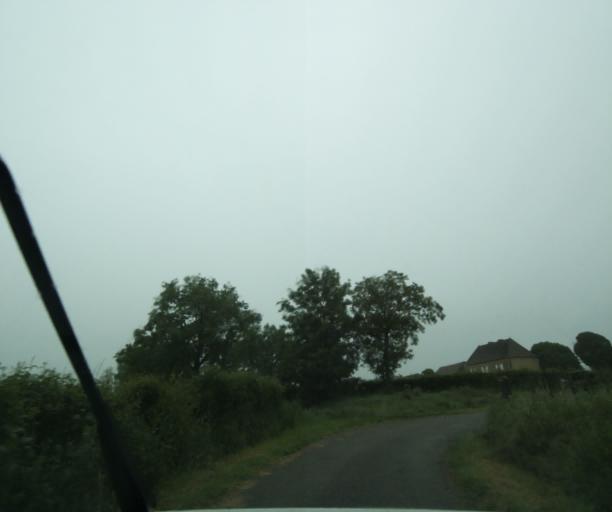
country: FR
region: Bourgogne
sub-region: Departement de Saone-et-Loire
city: Charolles
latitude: 46.3931
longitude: 4.2296
